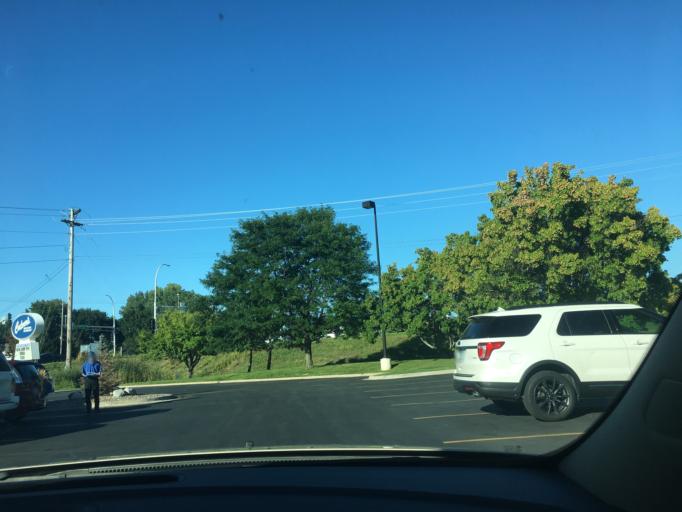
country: US
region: Minnesota
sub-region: Olmsted County
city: Rochester
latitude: 44.0789
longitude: -92.5118
